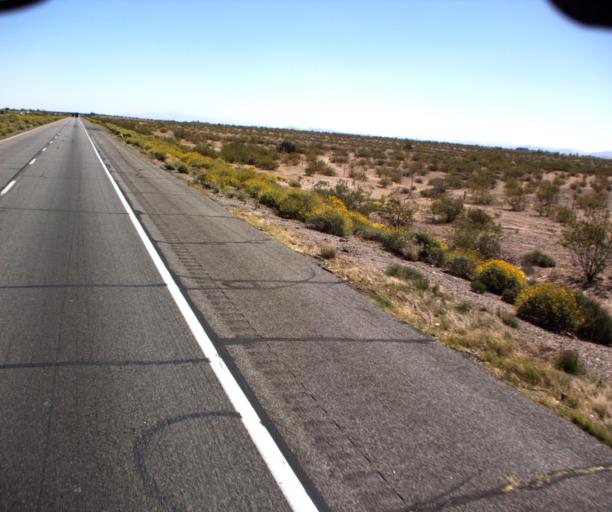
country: US
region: Arizona
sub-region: Maricopa County
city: Buckeye
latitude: 33.4726
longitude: -112.8269
